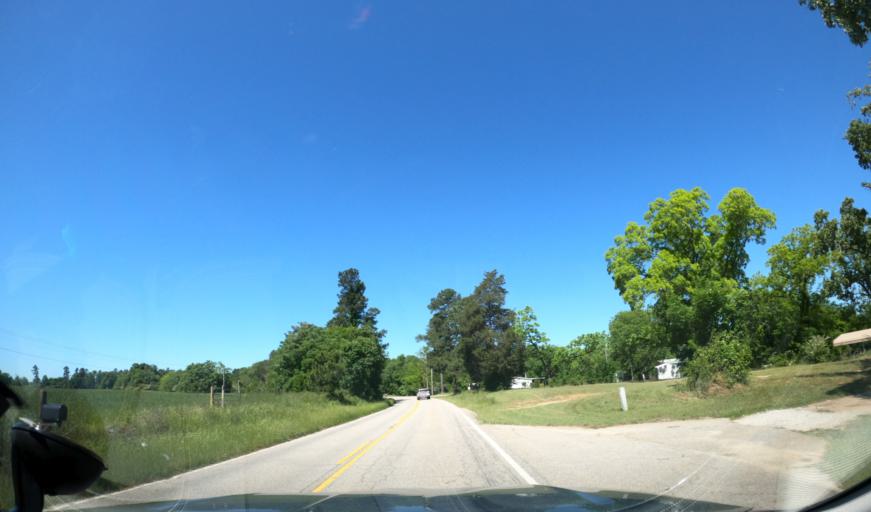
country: US
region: South Carolina
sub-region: Aiken County
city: Clearwater
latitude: 33.4662
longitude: -81.8661
